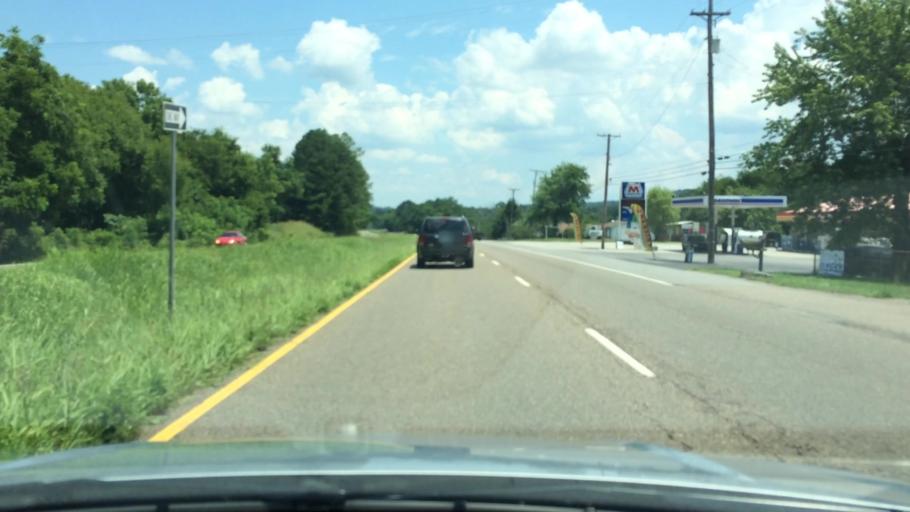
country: US
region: Tennessee
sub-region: Jefferson County
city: New Market
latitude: 36.0710
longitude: -83.6407
